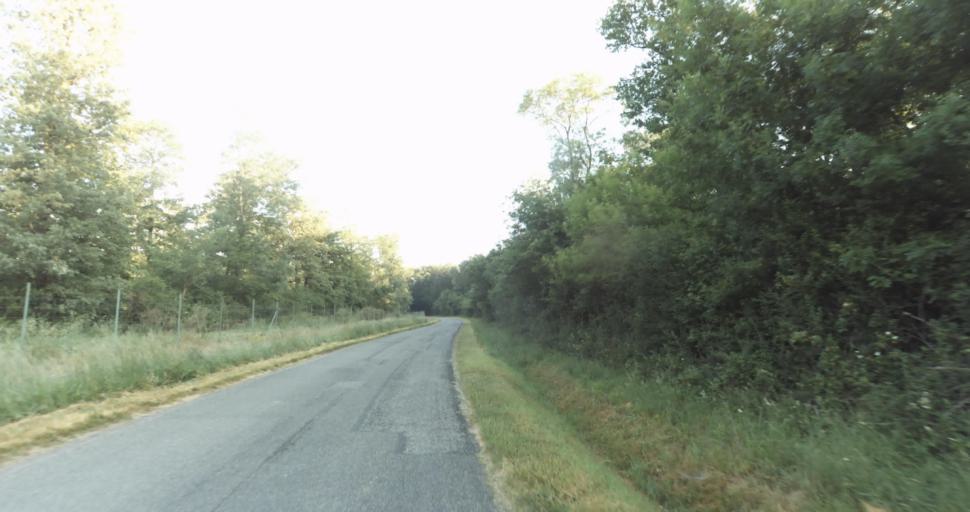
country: FR
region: Midi-Pyrenees
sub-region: Departement de la Haute-Garonne
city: Fontenilles
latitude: 43.5707
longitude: 1.1899
